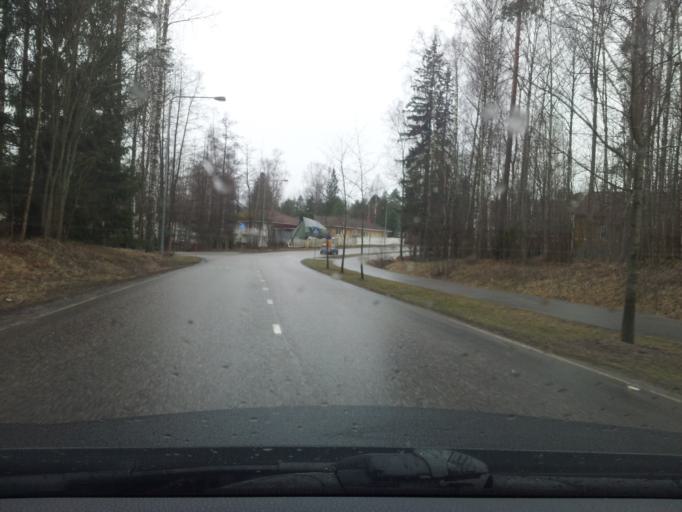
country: FI
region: Uusimaa
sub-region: Helsinki
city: Espoo
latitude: 60.1641
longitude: 24.6813
